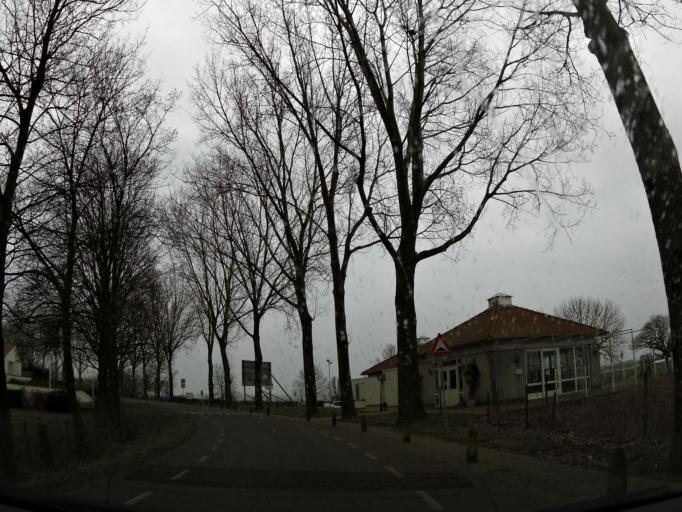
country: BE
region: Flanders
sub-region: Provincie Limburg
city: Maaseik
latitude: 51.1110
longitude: 5.8188
